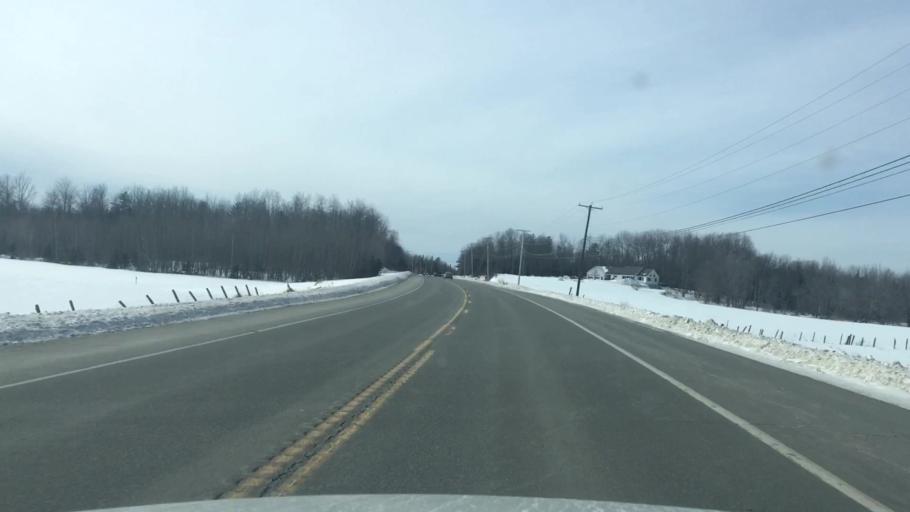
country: US
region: Maine
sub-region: Penobscot County
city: Kenduskeag
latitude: 44.9112
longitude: -68.9001
